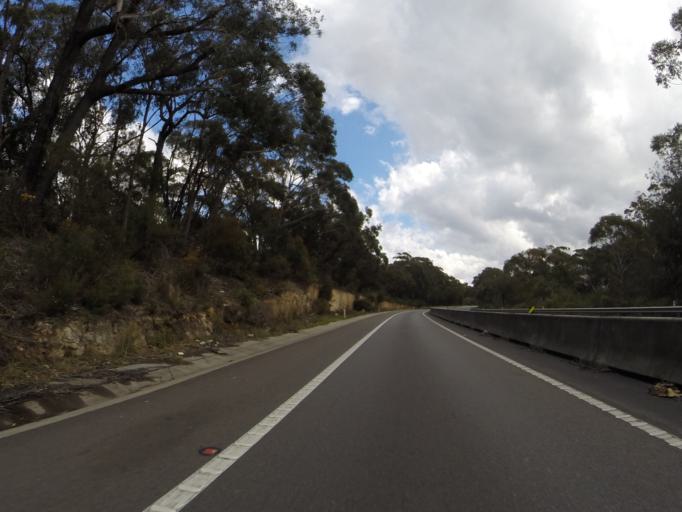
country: AU
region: New South Wales
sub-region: Wollongong
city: Mount Keira
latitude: -34.3494
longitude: 150.8005
